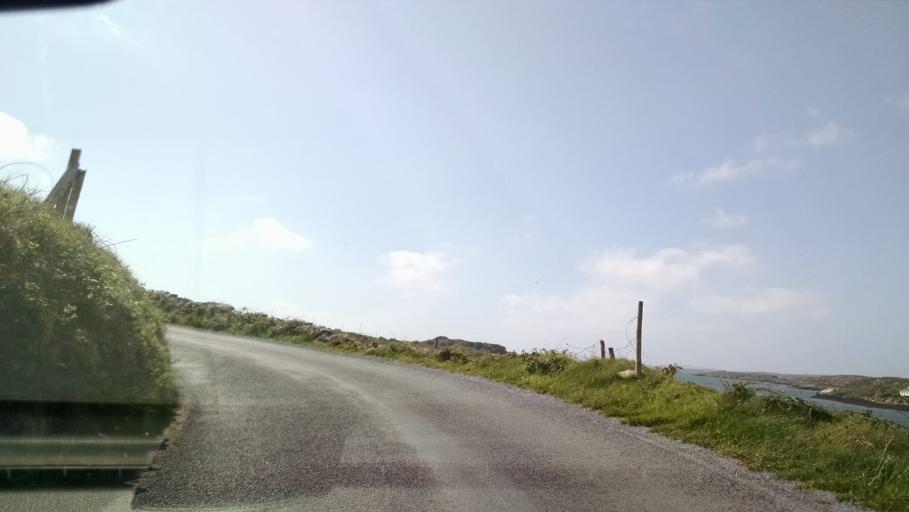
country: IE
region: Connaught
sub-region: County Galway
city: Clifden
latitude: 53.5114
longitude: -10.1122
